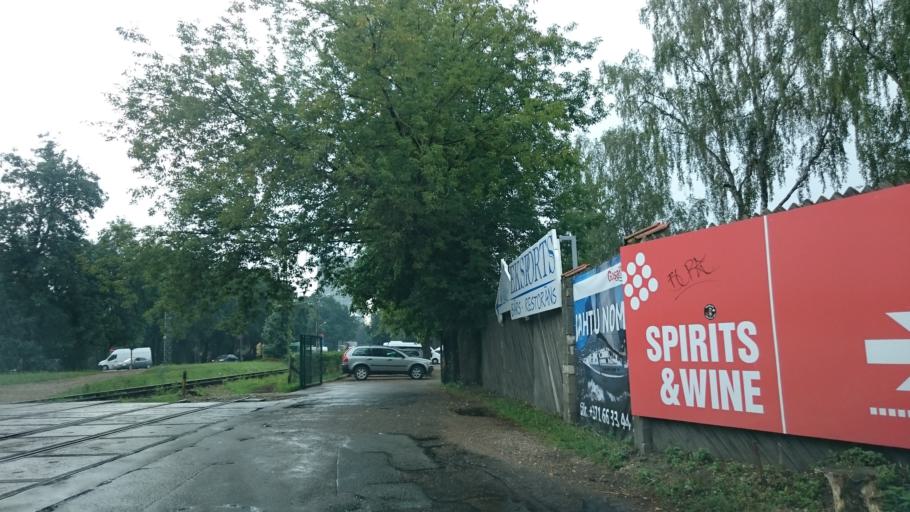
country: LV
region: Riga
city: Riga
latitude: 56.9600
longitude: 24.0977
